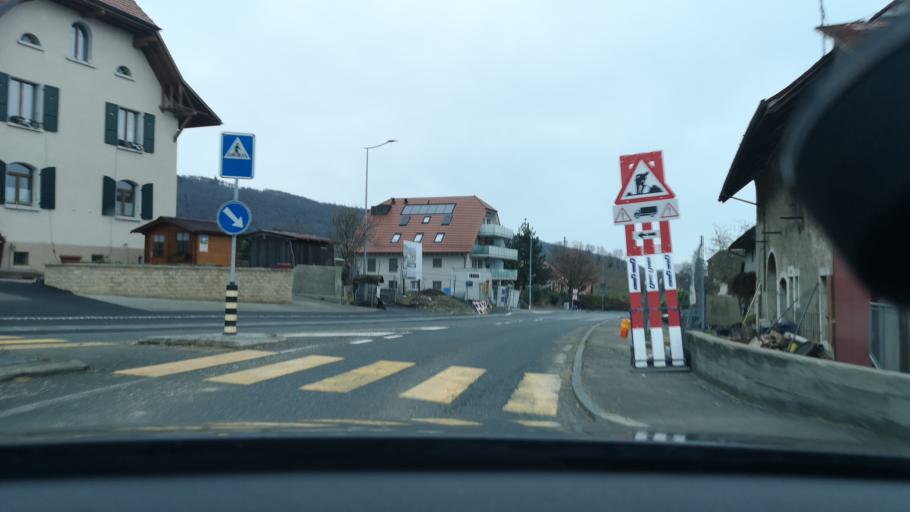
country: CH
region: Vaud
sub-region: Jura-Nord vaudois District
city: Yvonand
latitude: 46.8479
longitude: 6.7109
